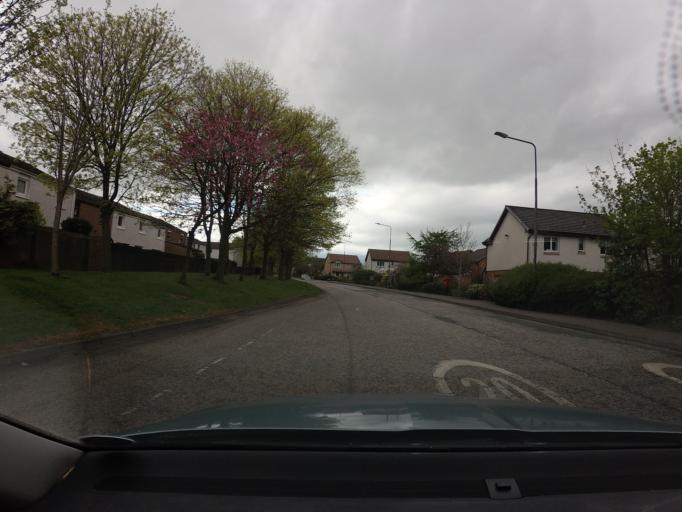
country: GB
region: Scotland
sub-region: Edinburgh
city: Queensferry
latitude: 55.9827
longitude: -3.3853
